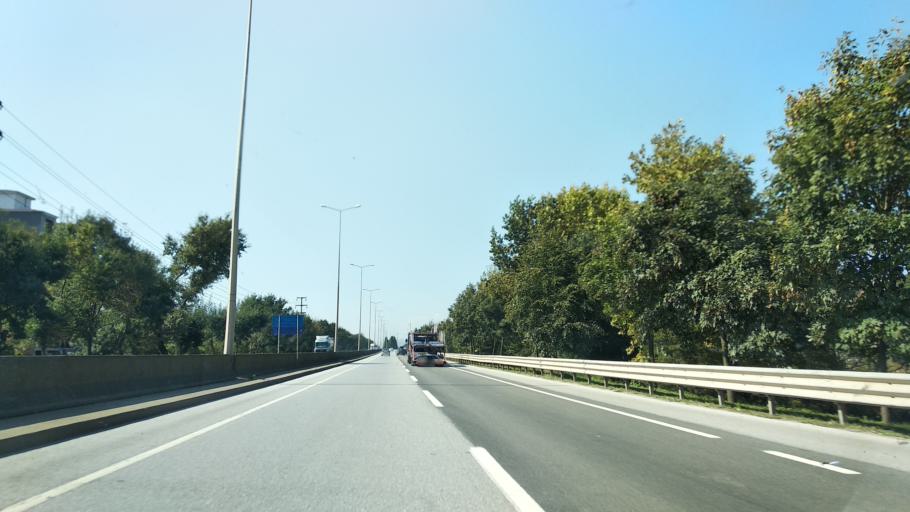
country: TR
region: Kocaeli
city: Kosekoy
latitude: 40.7544
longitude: 30.0169
